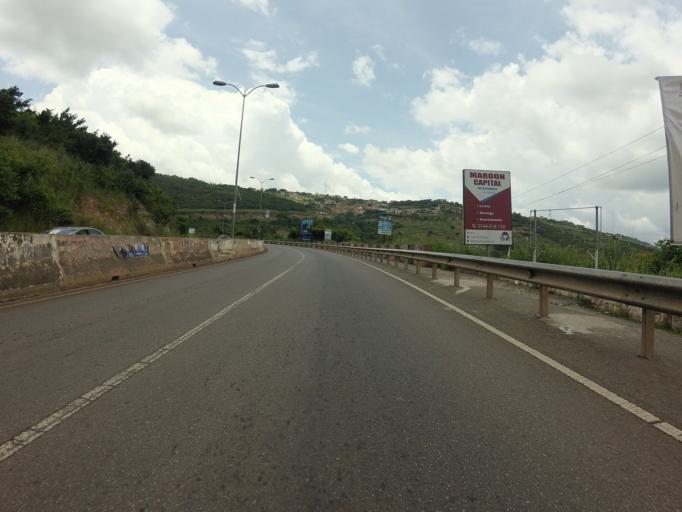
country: GH
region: Eastern
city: Aburi
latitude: 5.7874
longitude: -0.1839
